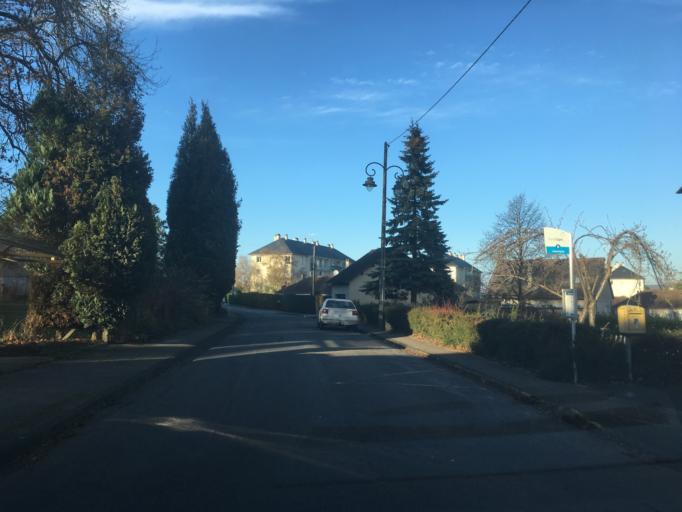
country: FR
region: Haute-Normandie
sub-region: Departement de l'Eure
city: Saint-Marcel
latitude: 49.1020
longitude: 1.4434
